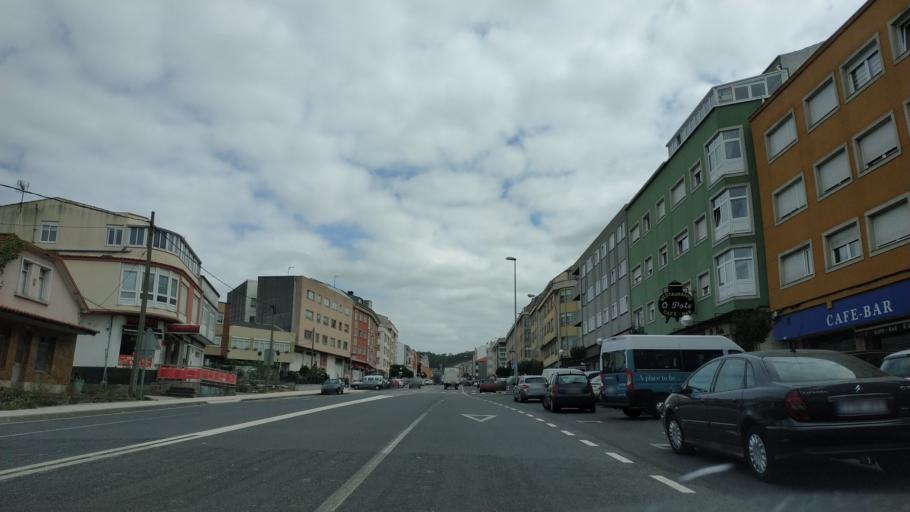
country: ES
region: Galicia
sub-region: Provincia da Coruna
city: Arteixo
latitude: 43.3173
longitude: -8.4878
